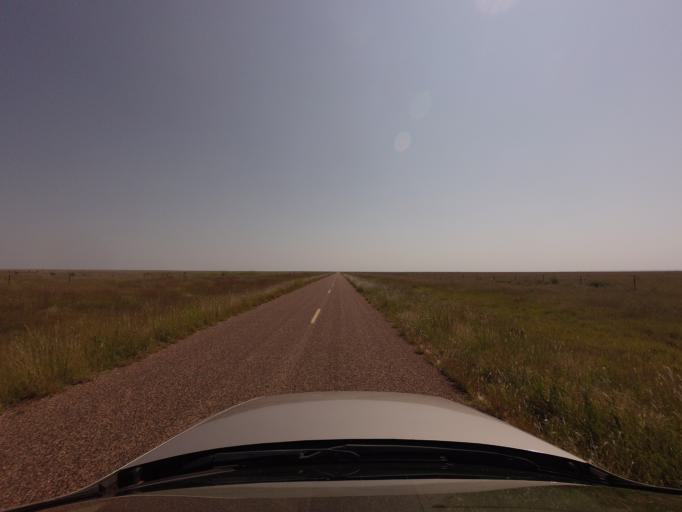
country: US
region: New Mexico
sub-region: Curry County
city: Cannon Air Force Base
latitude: 34.6332
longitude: -103.4355
